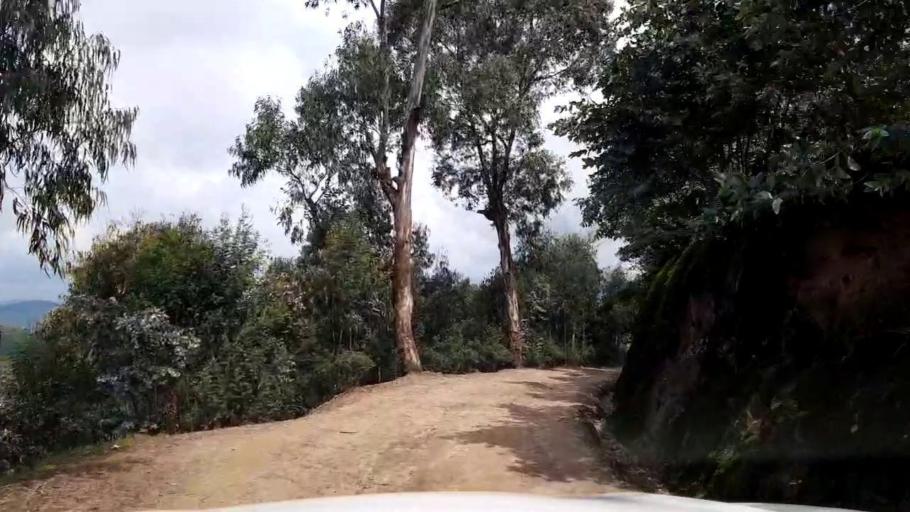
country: RW
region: Western Province
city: Kibuye
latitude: -1.9437
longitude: 29.4698
